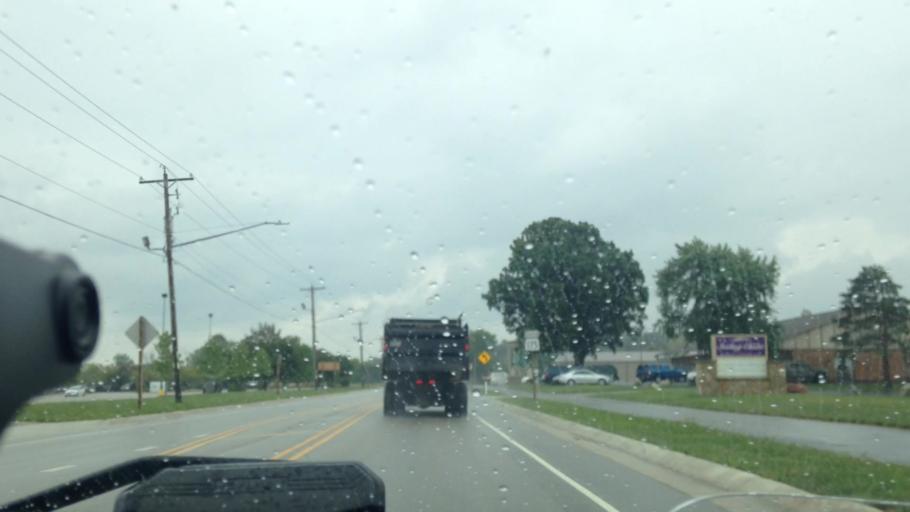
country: US
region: Wisconsin
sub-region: Washington County
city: Richfield
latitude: 43.2353
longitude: -88.1860
